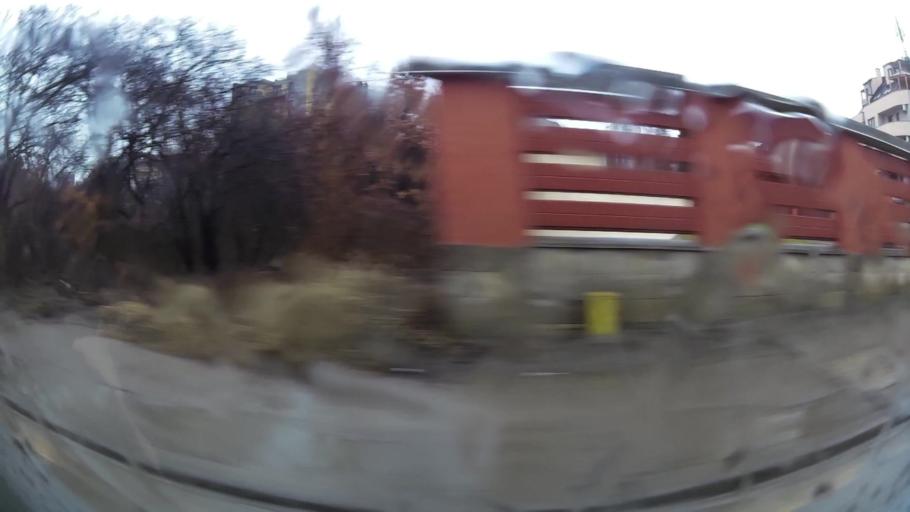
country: BG
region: Sofia-Capital
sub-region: Stolichna Obshtina
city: Sofia
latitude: 42.6543
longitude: 23.3363
